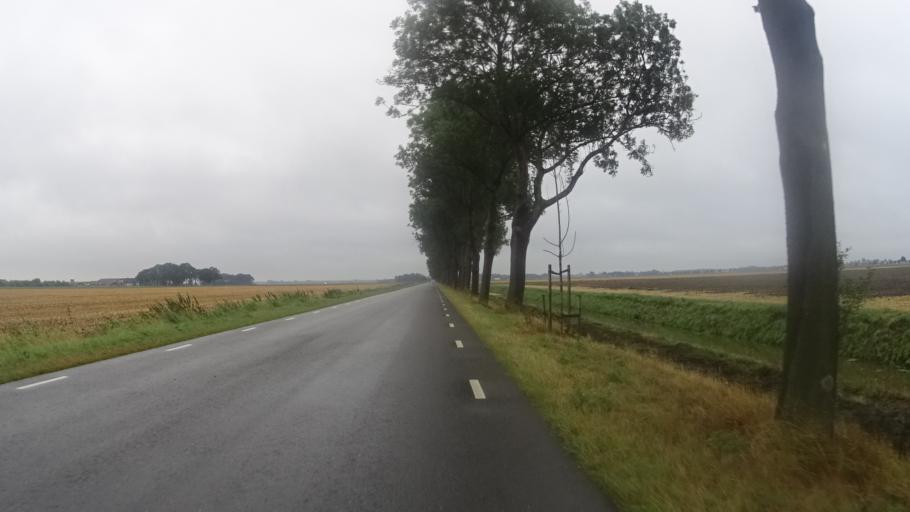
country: NL
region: Groningen
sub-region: Gemeente Veendam
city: Veendam
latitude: 53.1902
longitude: 6.9248
